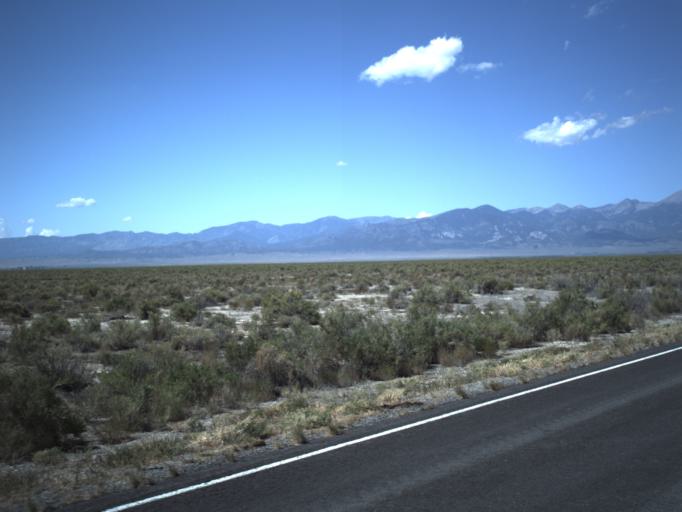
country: US
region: Nevada
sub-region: White Pine County
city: McGill
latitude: 39.0469
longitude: -113.9154
